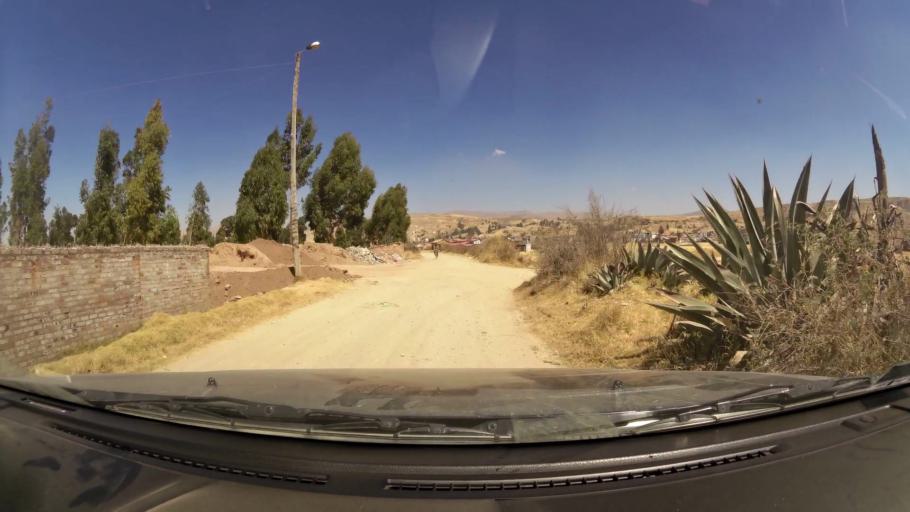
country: PE
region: Junin
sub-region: Provincia de Jauja
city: Jauja
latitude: -11.7637
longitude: -75.4960
